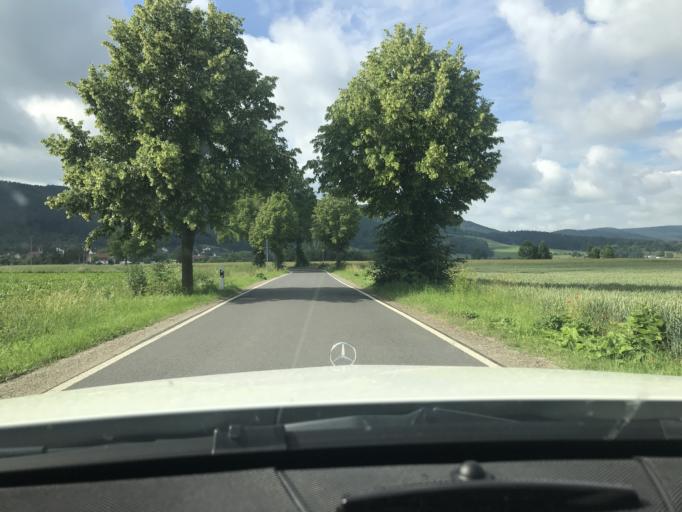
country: DE
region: Hesse
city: Wanfried
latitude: 51.1861
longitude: 10.1234
